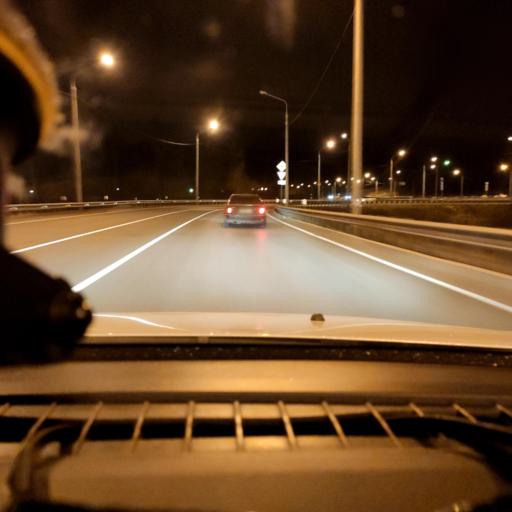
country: RU
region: Samara
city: Volzhskiy
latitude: 53.4347
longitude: 50.1127
